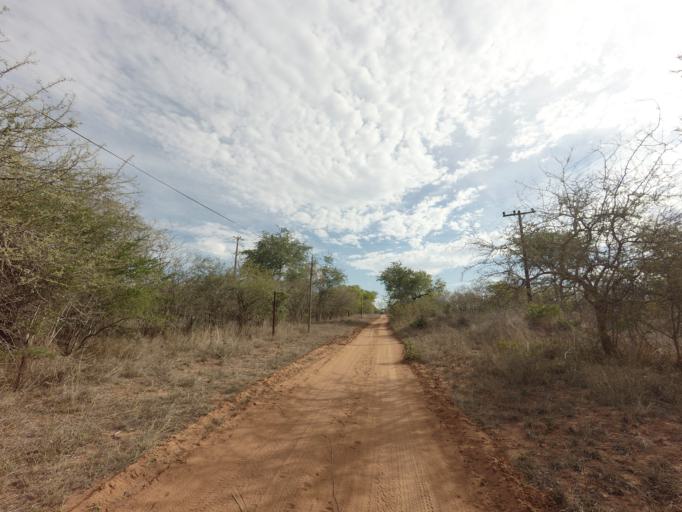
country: ZA
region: Limpopo
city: Thulamahashi
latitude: -24.5282
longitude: 31.1209
